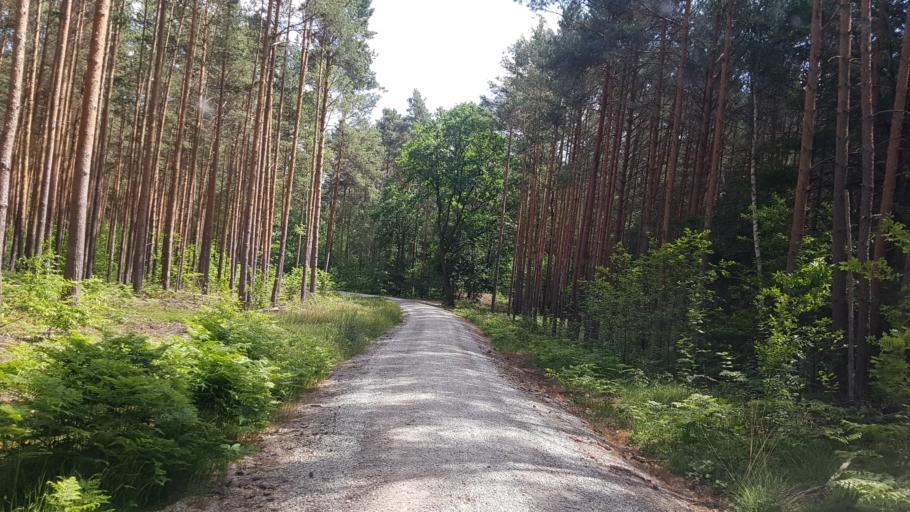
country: DE
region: Brandenburg
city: Plessa
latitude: 51.4958
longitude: 13.5945
